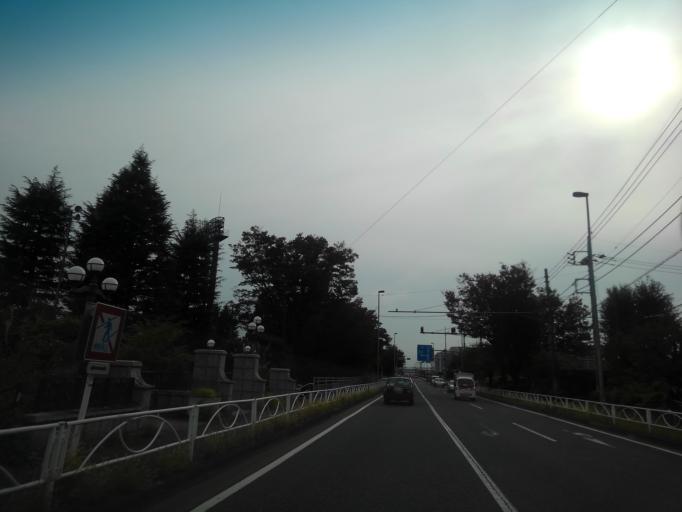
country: JP
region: Tokyo
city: Hino
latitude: 35.6855
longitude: 139.4141
